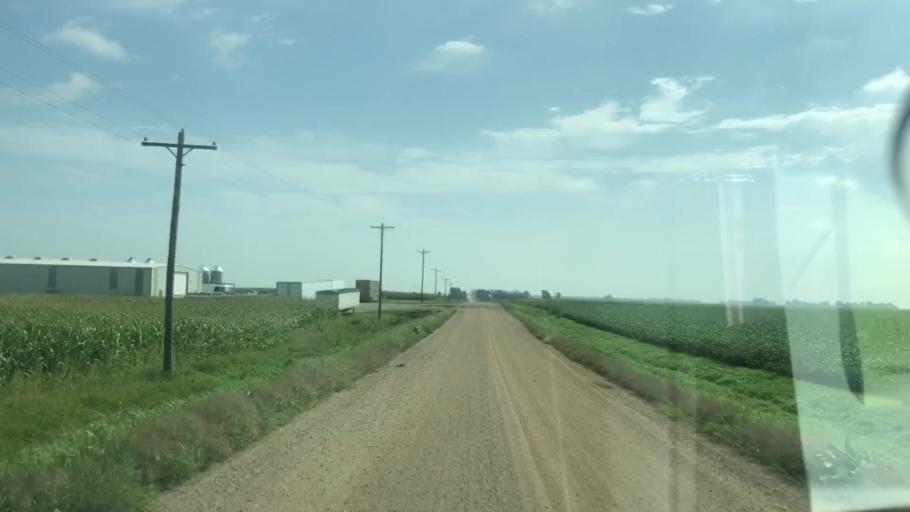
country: US
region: Iowa
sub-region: O'Brien County
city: Sheldon
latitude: 43.2153
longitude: -95.9752
